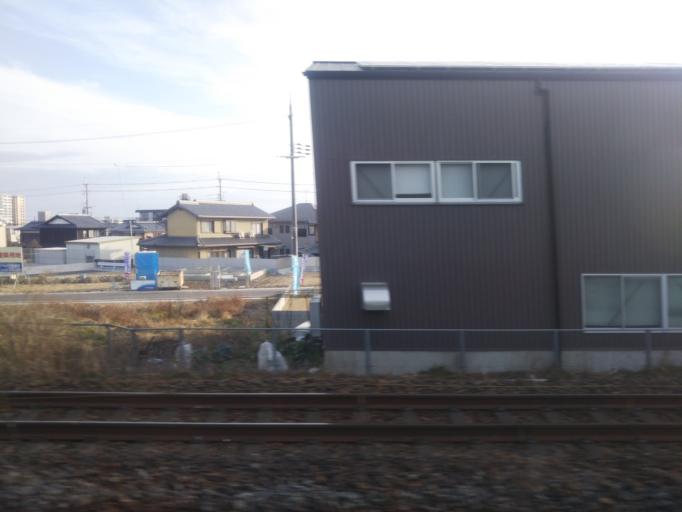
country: JP
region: Shiga Prefecture
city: Otsu-shi
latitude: 34.9851
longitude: 135.8920
